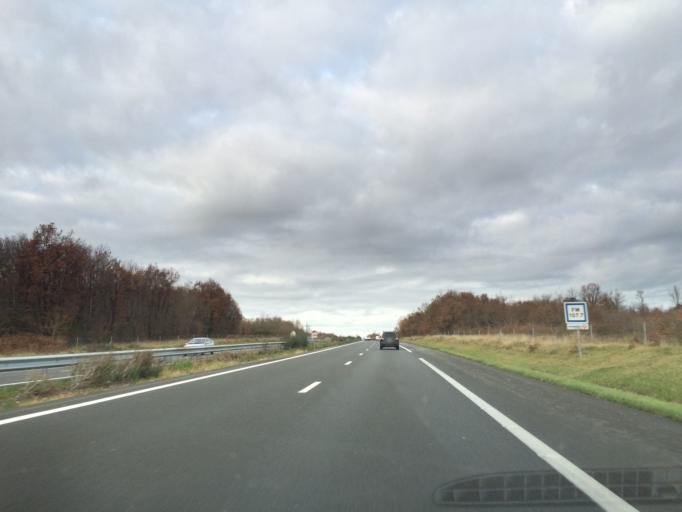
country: FR
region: Poitou-Charentes
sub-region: Departement des Deux-Sevres
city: Beauvoir-sur-Niort
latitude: 46.0854
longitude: -0.5312
